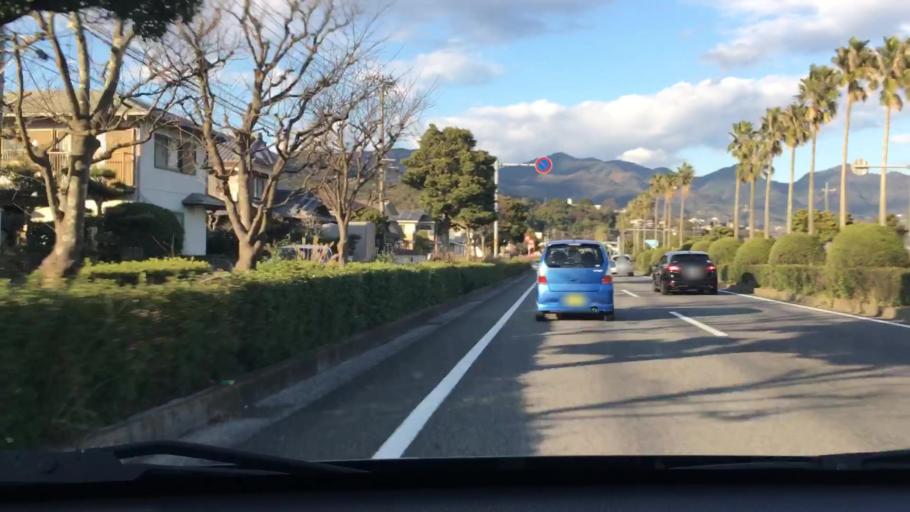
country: JP
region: Oita
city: Hiji
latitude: 33.3397
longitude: 131.4943
